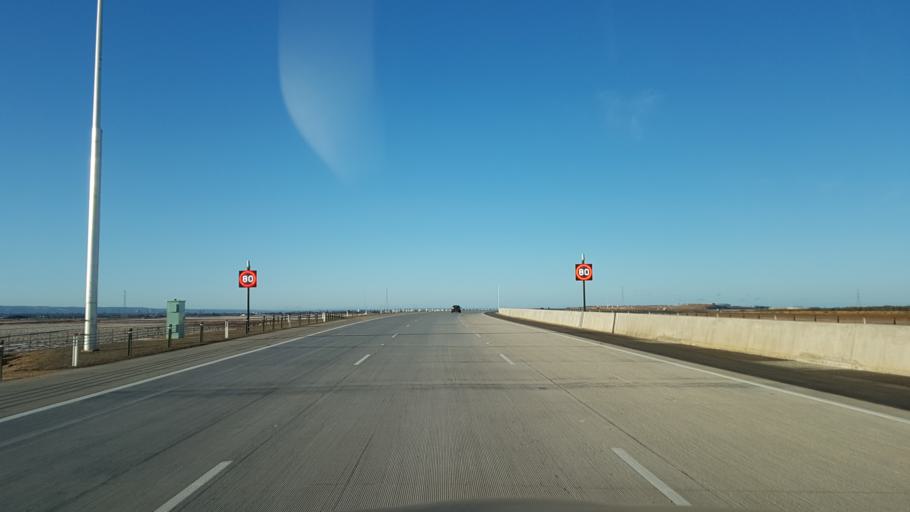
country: AU
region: South Australia
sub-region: Port Adelaide Enfield
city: Enfield
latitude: -34.7995
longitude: 138.5770
